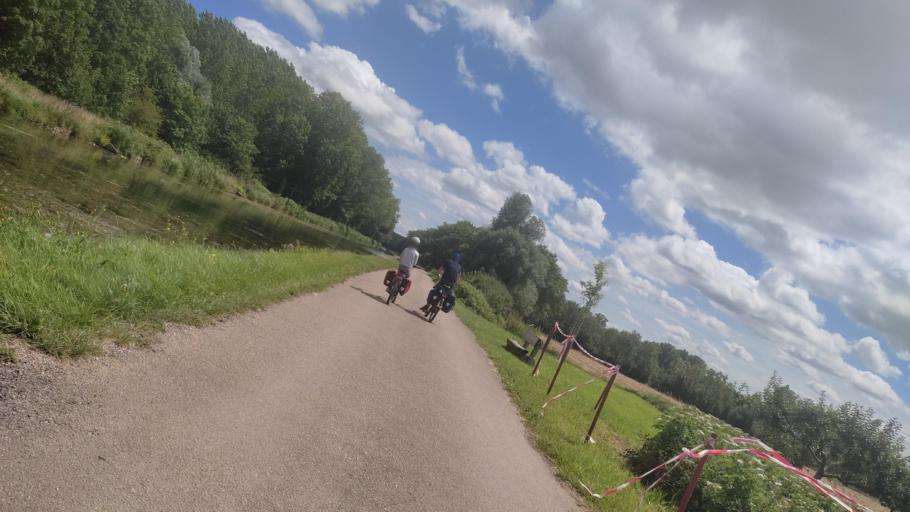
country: FR
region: Bourgogne
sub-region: Departement de l'Yonne
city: Flogny-la-Chapelle
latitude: 47.9323
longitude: 3.9112
